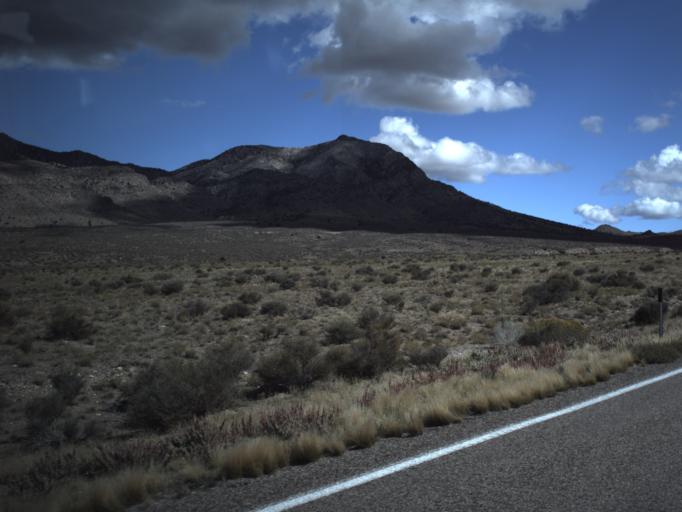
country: US
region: Utah
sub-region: Beaver County
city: Milford
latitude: 38.4419
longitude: -113.3206
